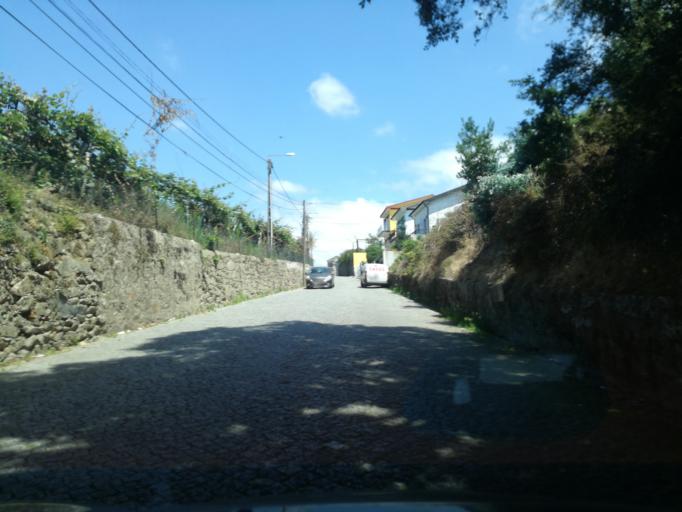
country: PT
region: Porto
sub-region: Maia
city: Maia
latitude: 41.2432
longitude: -8.6084
